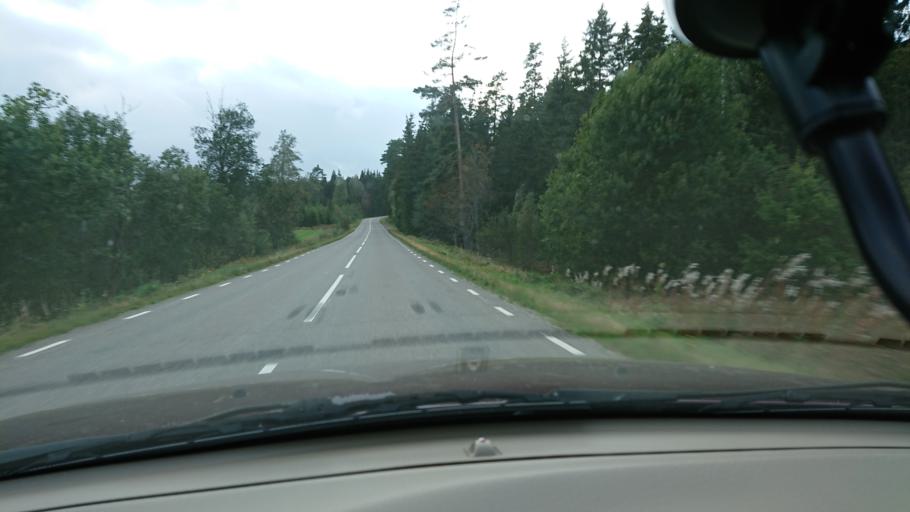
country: SE
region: Kronoberg
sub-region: Vaxjo Kommun
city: Lammhult
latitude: 57.0938
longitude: 14.6896
